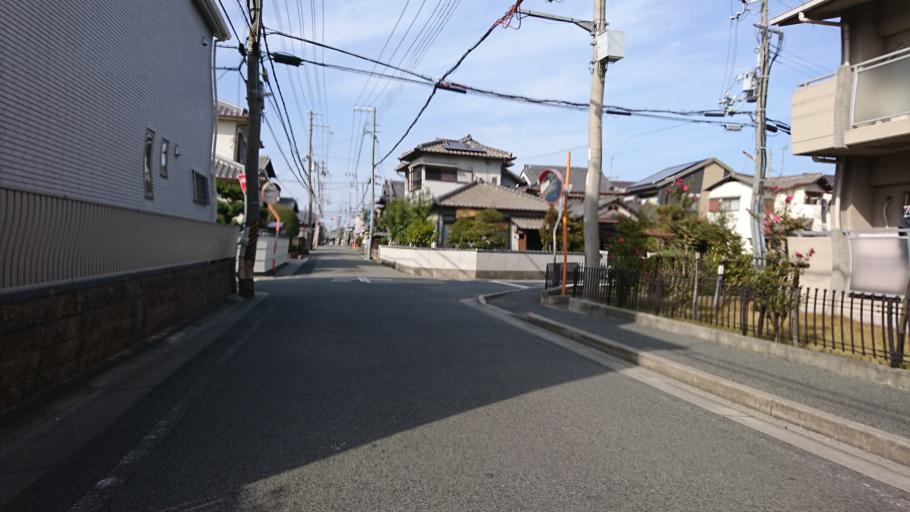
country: JP
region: Hyogo
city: Kakogawacho-honmachi
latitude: 34.7420
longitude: 134.8278
